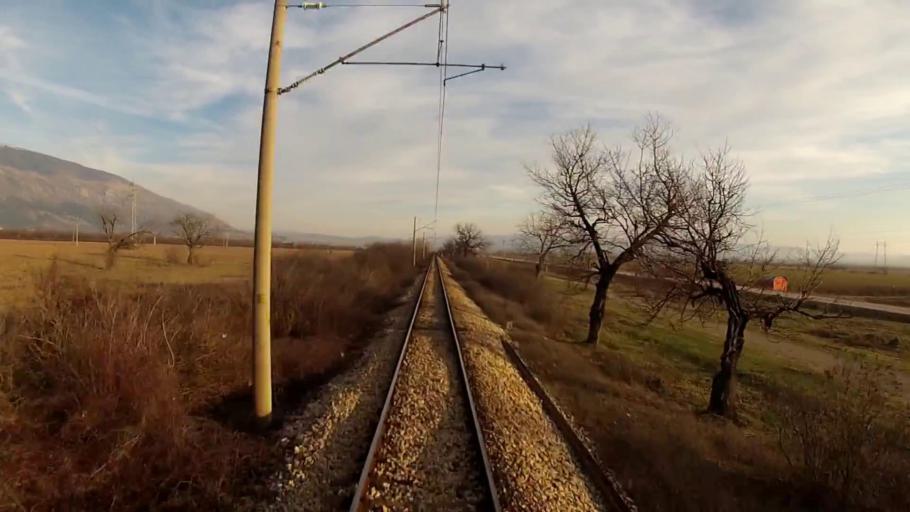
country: BG
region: Plovdiv
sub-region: Obshtina Karlovo
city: Karlovo
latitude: 42.6334
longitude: 24.7727
